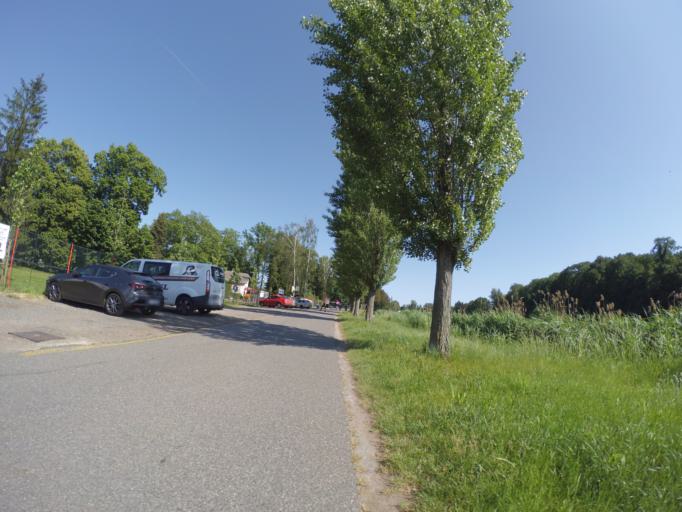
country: CZ
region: Central Bohemia
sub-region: Okres Nymburk
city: Nymburk
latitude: 50.1845
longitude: 15.0532
